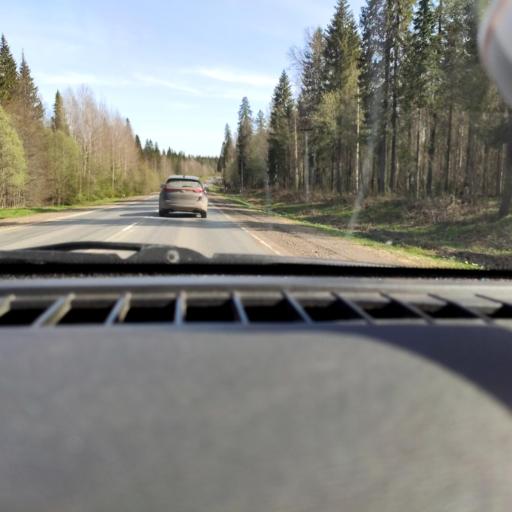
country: RU
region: Perm
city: Perm
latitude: 58.2056
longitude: 56.1982
